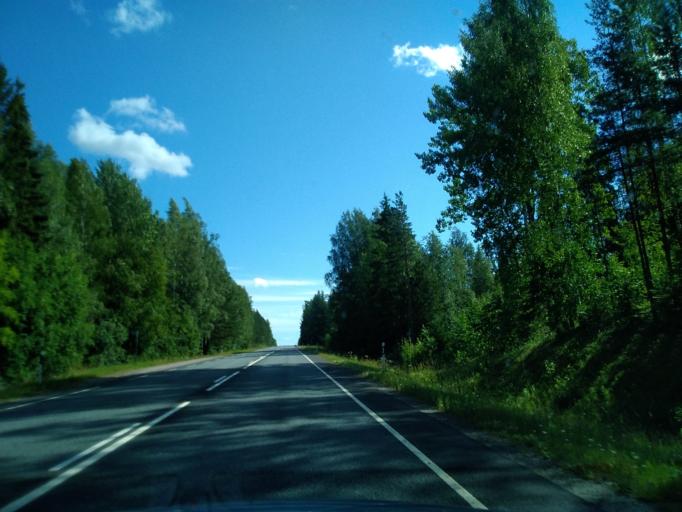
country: FI
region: Haeme
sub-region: Haemeenlinna
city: Renko
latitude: 60.8404
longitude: 24.1002
